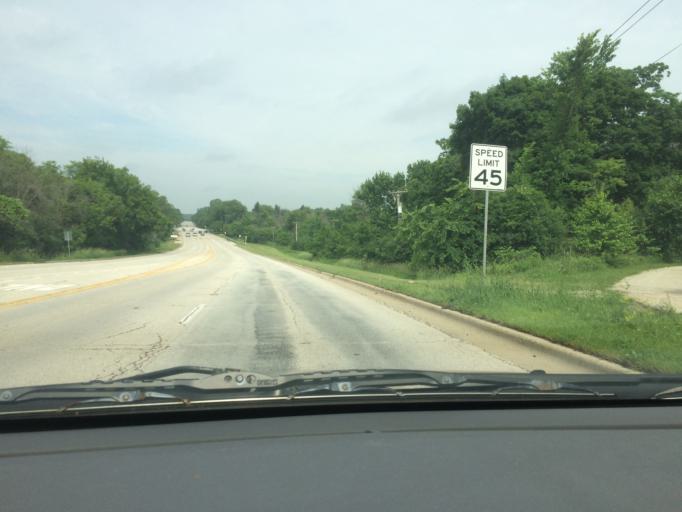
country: US
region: Illinois
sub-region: Cook County
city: Bartlett
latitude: 41.9439
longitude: -88.1778
